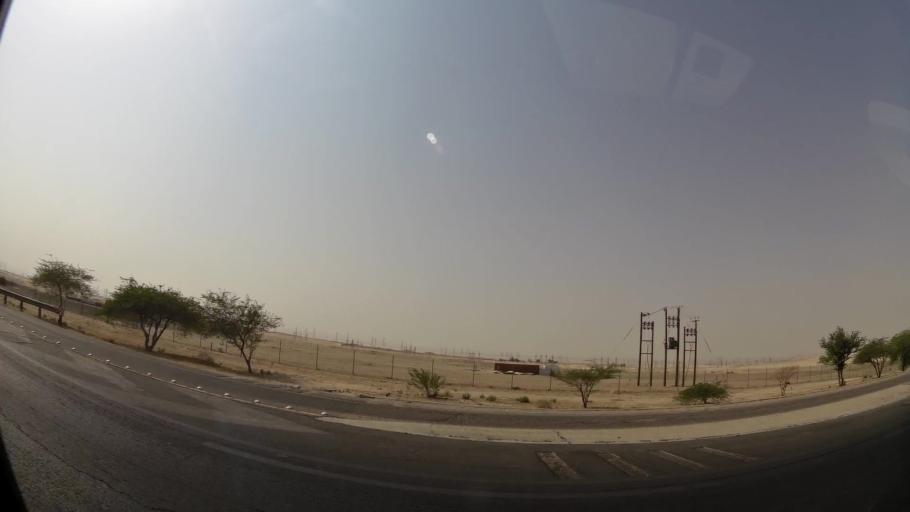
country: KW
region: Muhafazat al Jahra'
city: Al Jahra'
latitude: 29.3229
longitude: 47.6395
